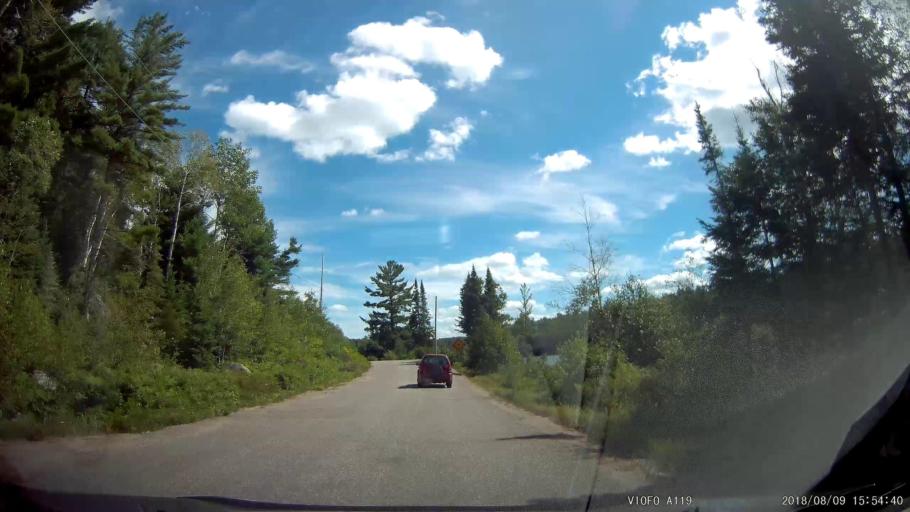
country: CA
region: Ontario
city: Rayside-Balfour
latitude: 46.6074
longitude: -81.5282
